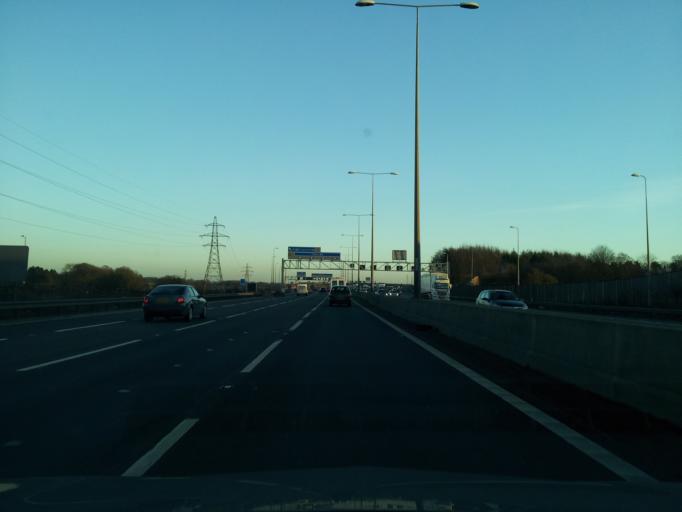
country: GB
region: England
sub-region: Luton
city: Luton
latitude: 51.8606
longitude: -0.4309
